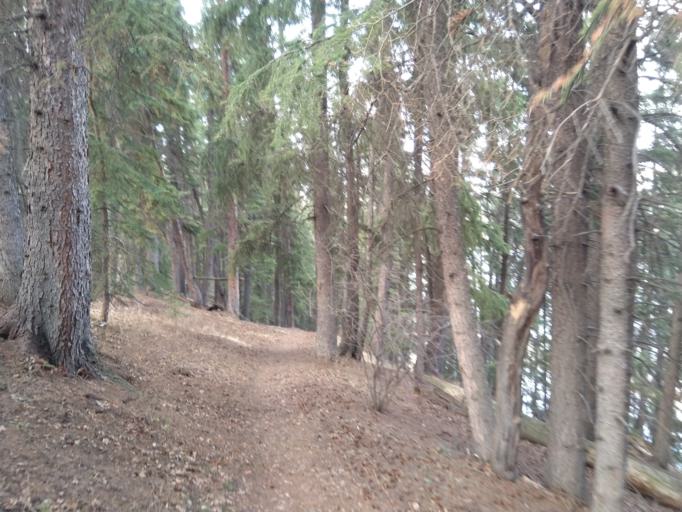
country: CA
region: Alberta
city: Cochrane
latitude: 51.1885
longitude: -114.5087
